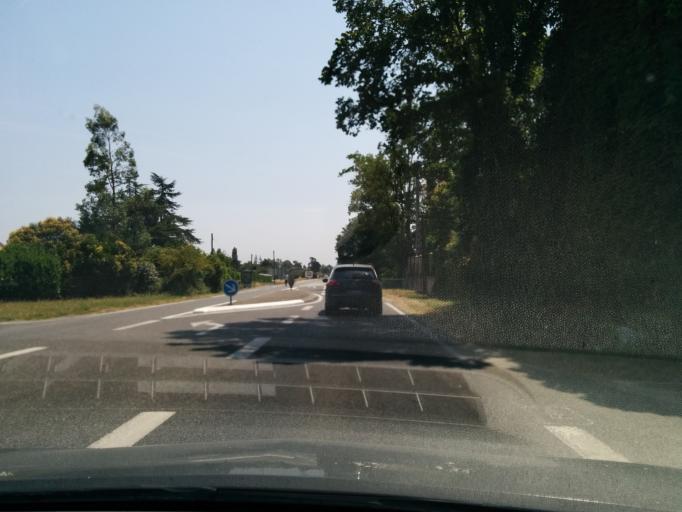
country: FR
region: Midi-Pyrenees
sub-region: Departement de la Haute-Garonne
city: Pechabou
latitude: 43.4997
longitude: 1.5149
